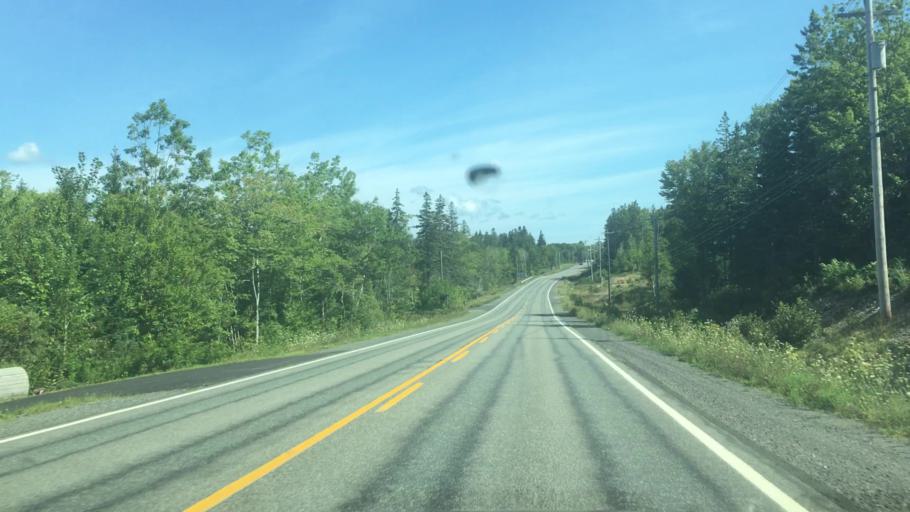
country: CA
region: Nova Scotia
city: Sydney
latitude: 45.9919
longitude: -60.4112
